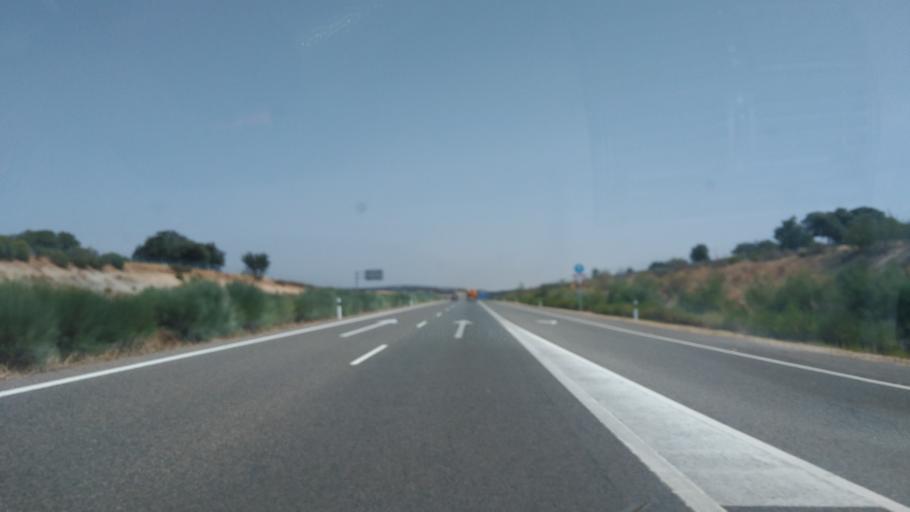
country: ES
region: Castille and Leon
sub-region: Provincia de Salamanca
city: San Munoz
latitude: 40.8222
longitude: -6.1155
